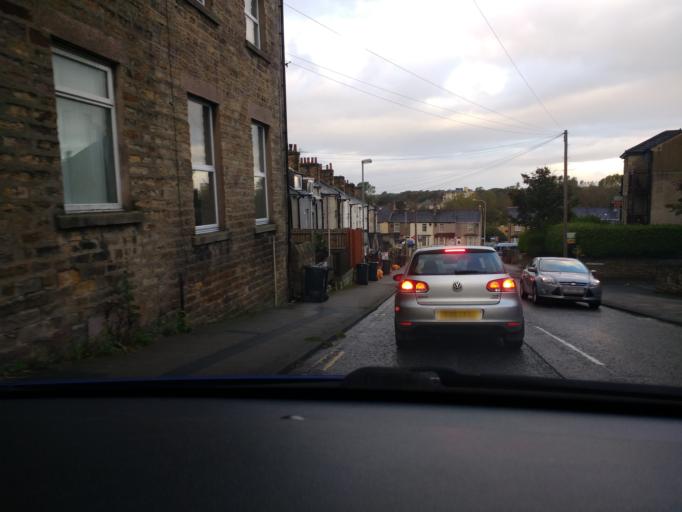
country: GB
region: England
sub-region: Lancashire
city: Lancaster
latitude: 54.0533
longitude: -2.7916
